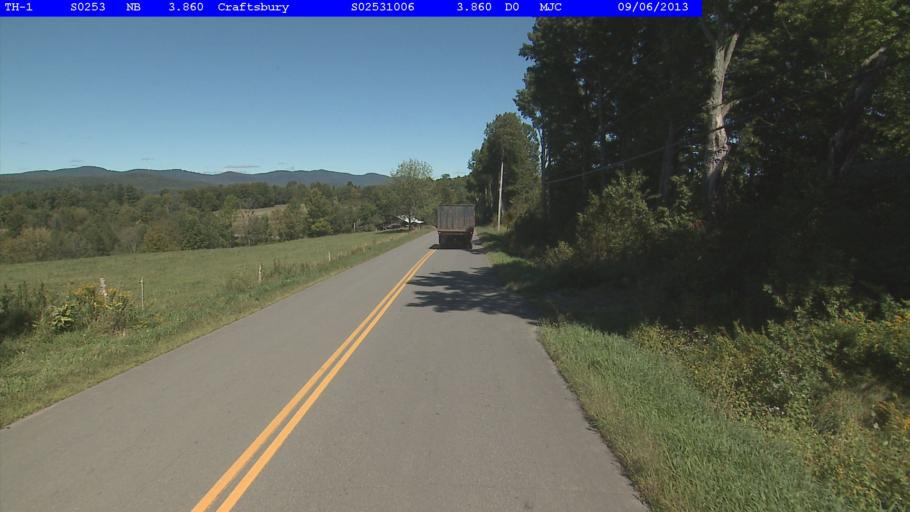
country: US
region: Vermont
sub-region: Caledonia County
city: Hardwick
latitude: 44.6638
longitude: -72.3835
